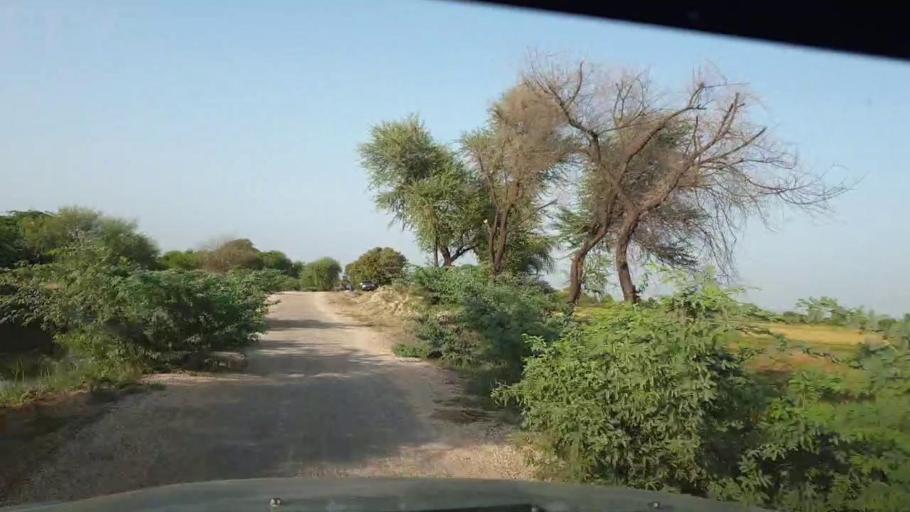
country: PK
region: Sindh
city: Rajo Khanani
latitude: 25.0251
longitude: 68.7707
